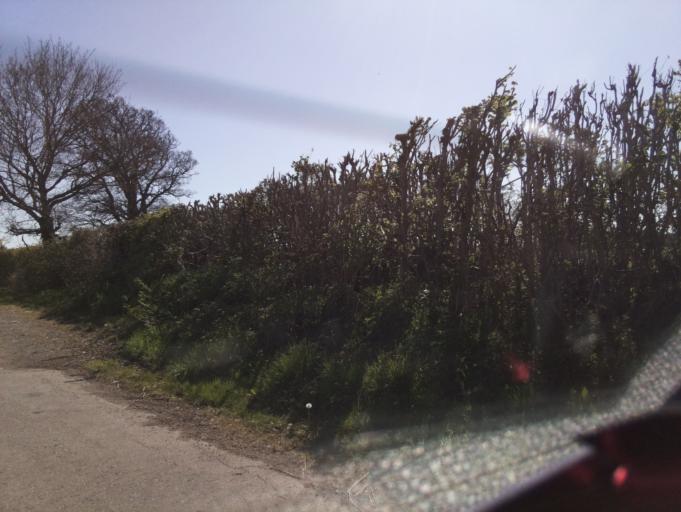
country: GB
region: England
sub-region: Gloucestershire
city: Berkeley
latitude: 51.6726
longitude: -2.4384
